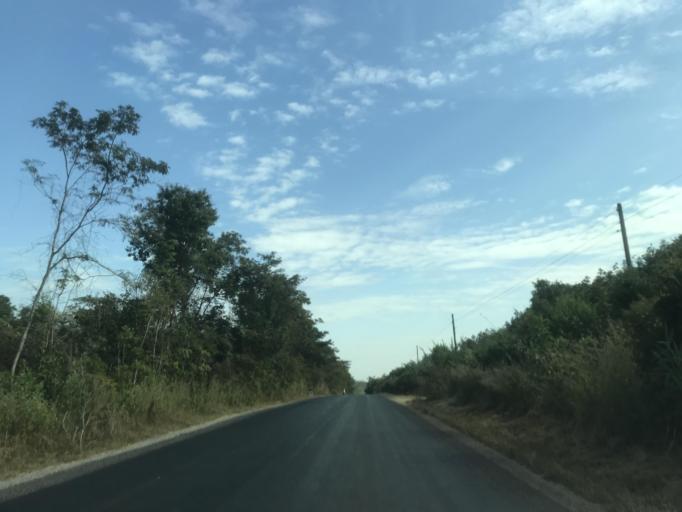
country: LA
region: Khammouan
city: Muang Hinboun
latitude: 17.8085
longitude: 104.4741
